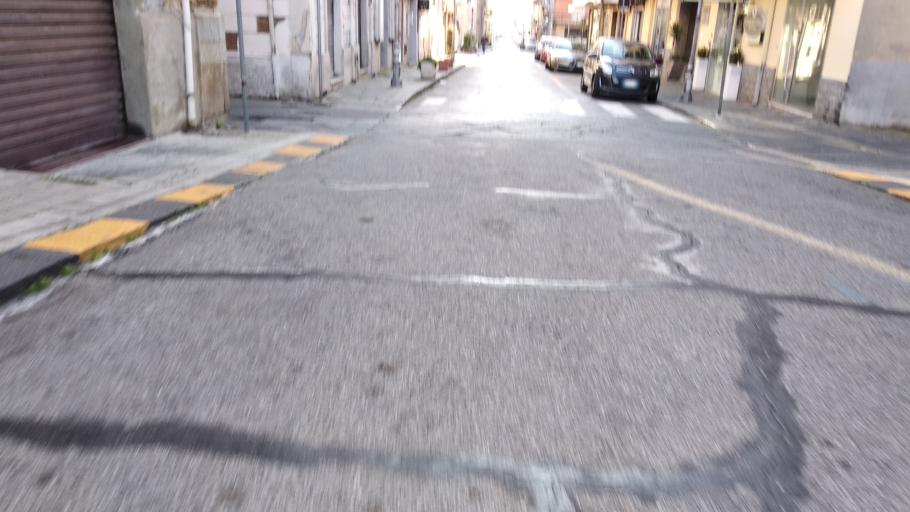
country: IT
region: Calabria
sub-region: Provincia di Reggio Calabria
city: Seminara
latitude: 38.3557
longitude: 15.8446
